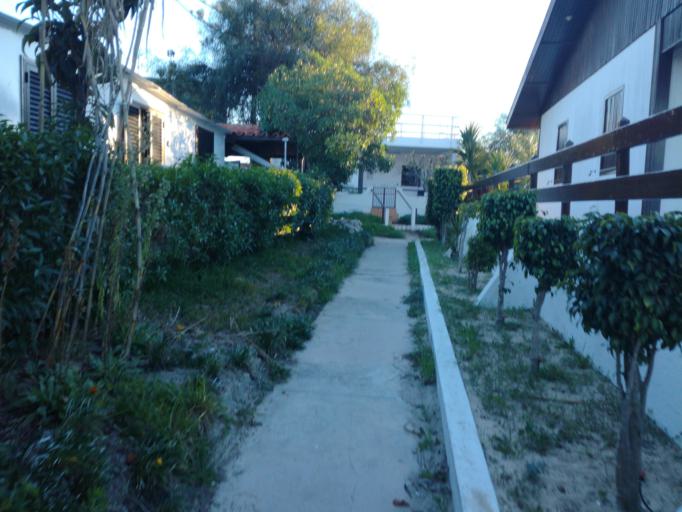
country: PT
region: Faro
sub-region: Olhao
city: Olhao
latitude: 37.0228
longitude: -7.8040
